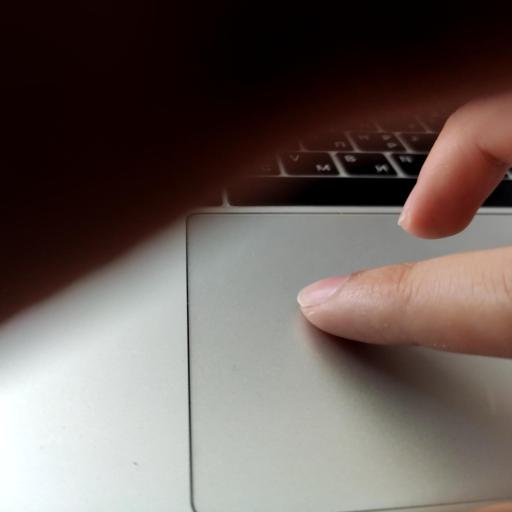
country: RU
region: Krasnodarskiy
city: Vysokoye
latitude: 43.4898
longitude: 39.9993
